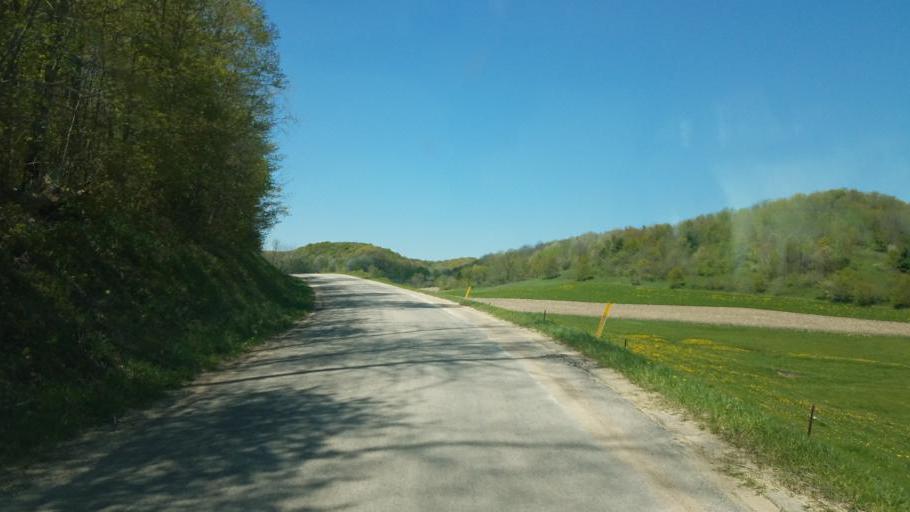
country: US
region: Wisconsin
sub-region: Vernon County
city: Hillsboro
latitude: 43.5979
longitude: -90.4474
